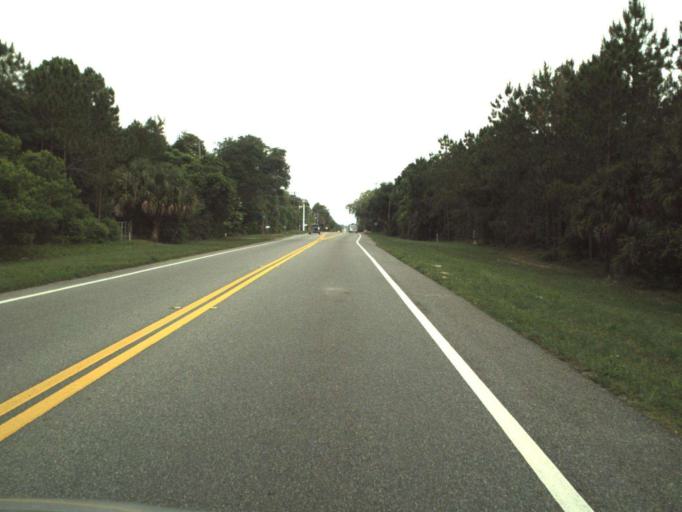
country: US
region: Florida
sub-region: Seminole County
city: Geneva
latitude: 28.7397
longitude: -81.1221
